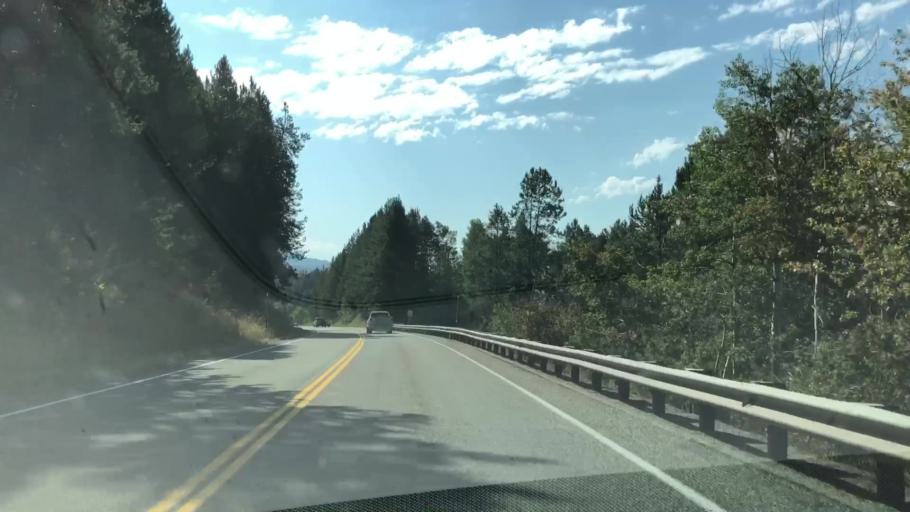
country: US
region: Idaho
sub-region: Teton County
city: Victor
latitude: 43.3044
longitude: -111.1343
